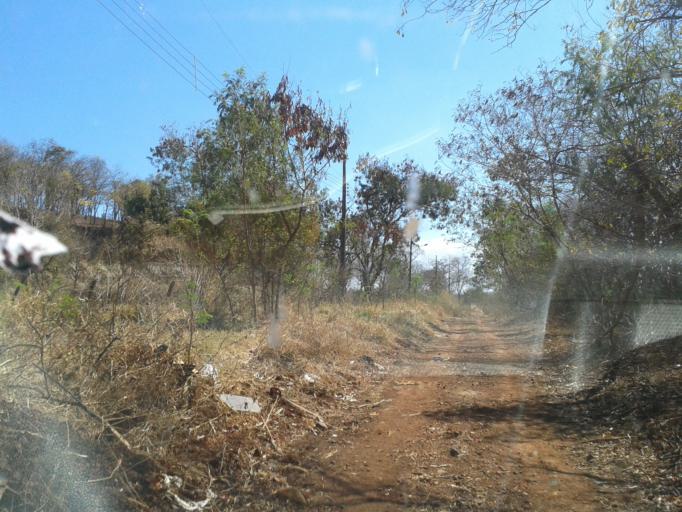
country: BR
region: Minas Gerais
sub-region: Capinopolis
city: Capinopolis
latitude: -18.6881
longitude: -49.5834
